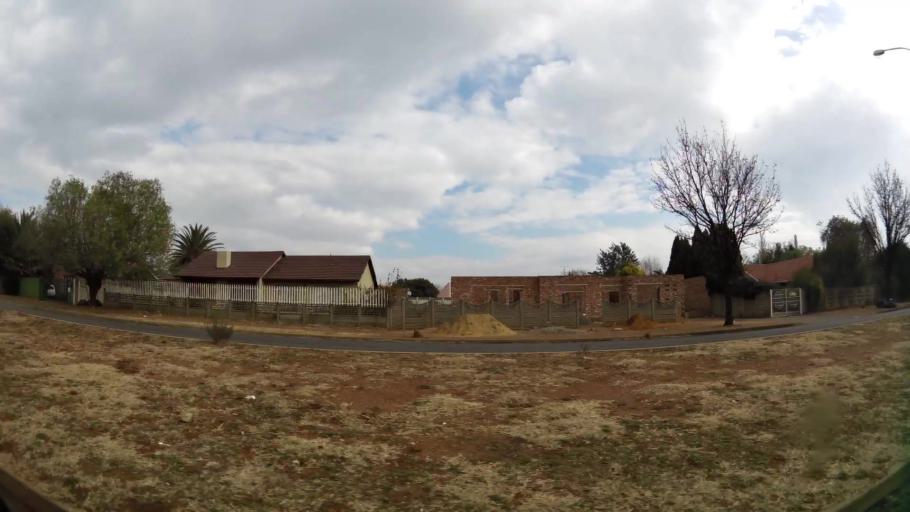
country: ZA
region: Gauteng
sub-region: Sedibeng District Municipality
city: Vanderbijlpark
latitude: -26.7191
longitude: 27.8631
